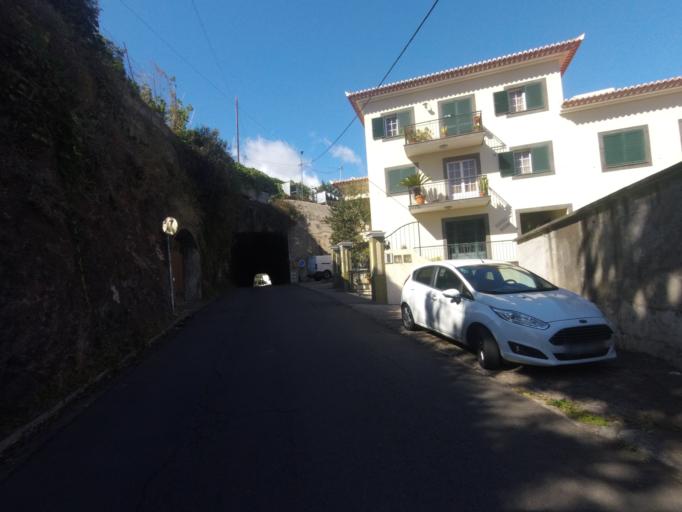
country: PT
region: Madeira
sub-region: Ribeira Brava
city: Campanario
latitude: 32.6744
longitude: -17.0318
